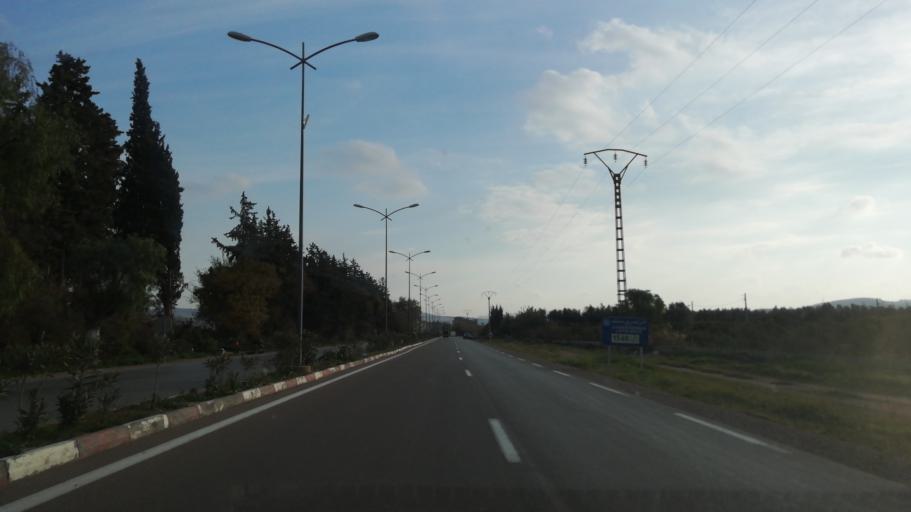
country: DZ
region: Mascara
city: Mascara
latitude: 35.6024
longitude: 0.0636
